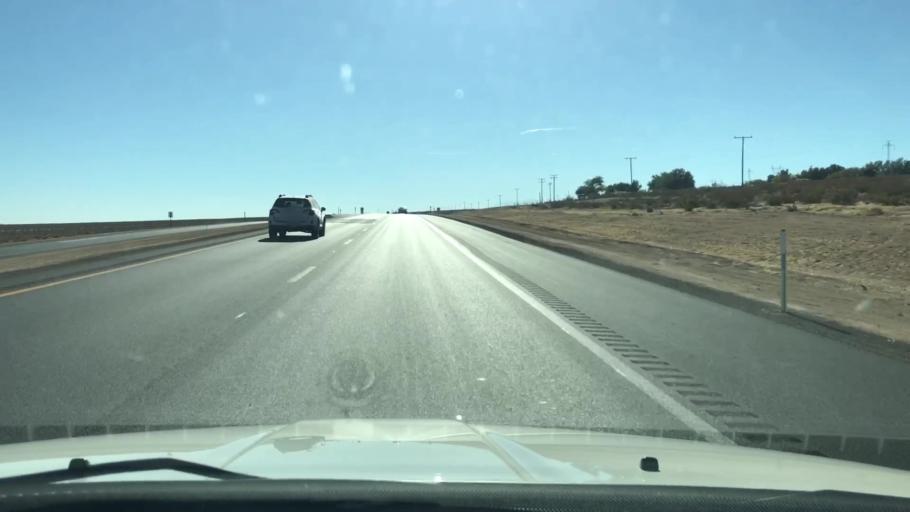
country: US
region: California
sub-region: Kern County
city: Inyokern
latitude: 35.6231
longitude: -117.8920
